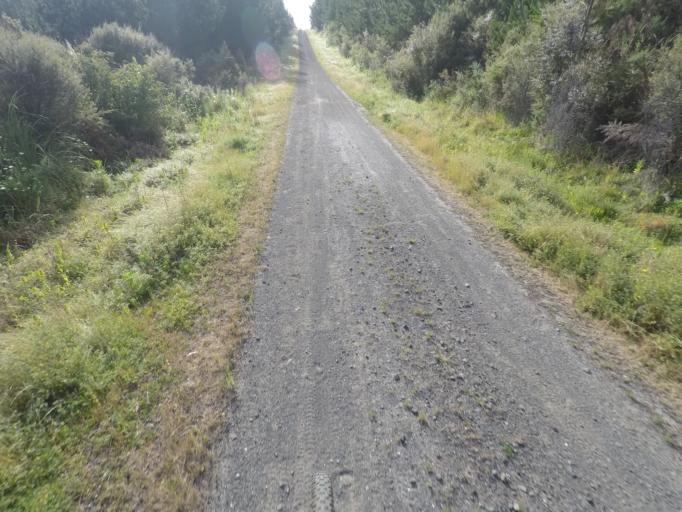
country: NZ
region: Auckland
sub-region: Auckland
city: Rothesay Bay
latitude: -36.7096
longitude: 174.5838
